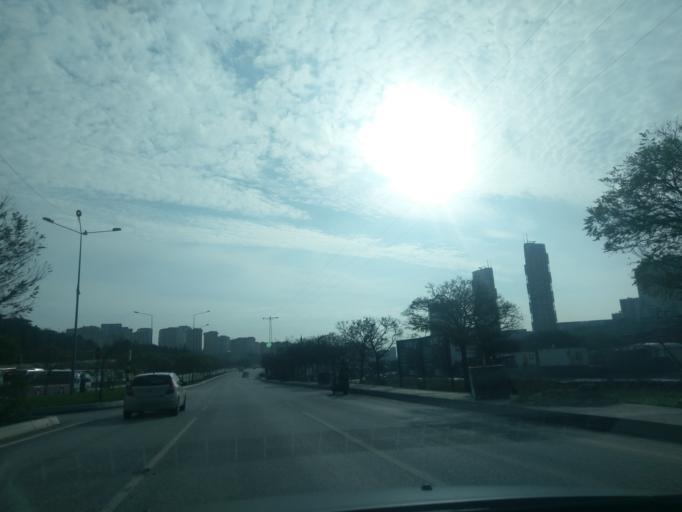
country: TR
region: Istanbul
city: Mahmutbey
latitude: 41.0471
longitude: 28.7740
